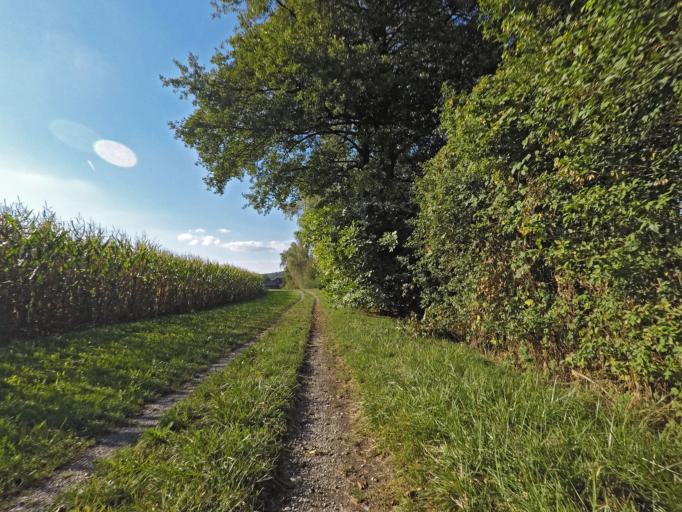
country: CH
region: Thurgau
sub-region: Frauenfeld District
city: Diessenhofen
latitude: 47.6637
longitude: 8.7465
